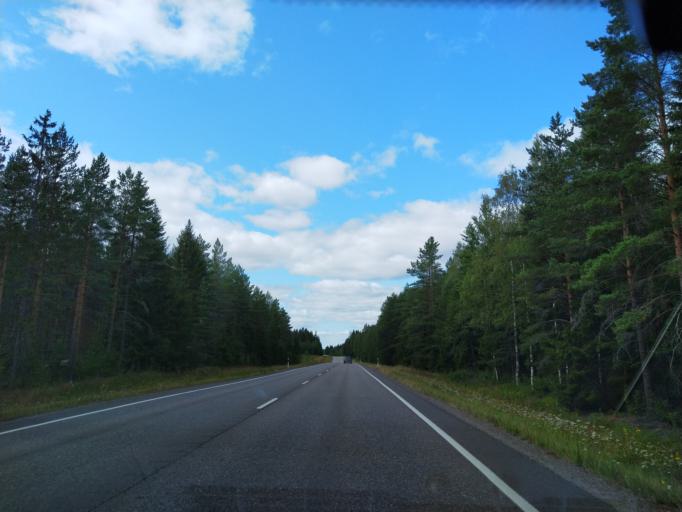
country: FI
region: Haeme
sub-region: Haemeenlinna
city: Renko
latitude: 60.7635
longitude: 24.2706
